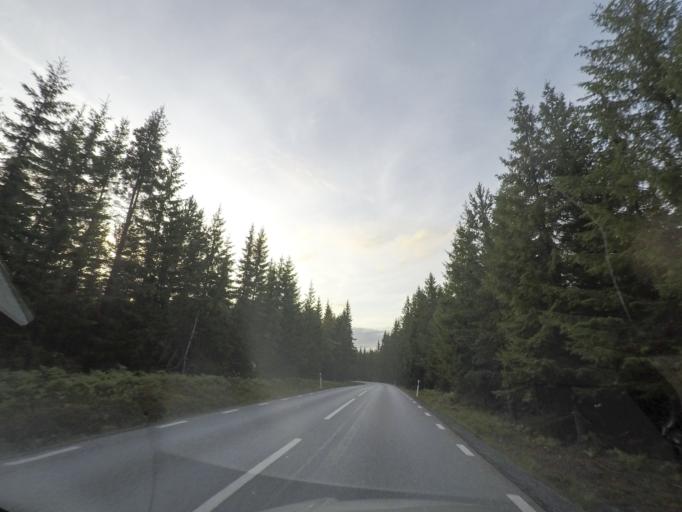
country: SE
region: OErebro
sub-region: Hallefors Kommun
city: Haellefors
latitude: 59.5962
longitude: 14.6736
